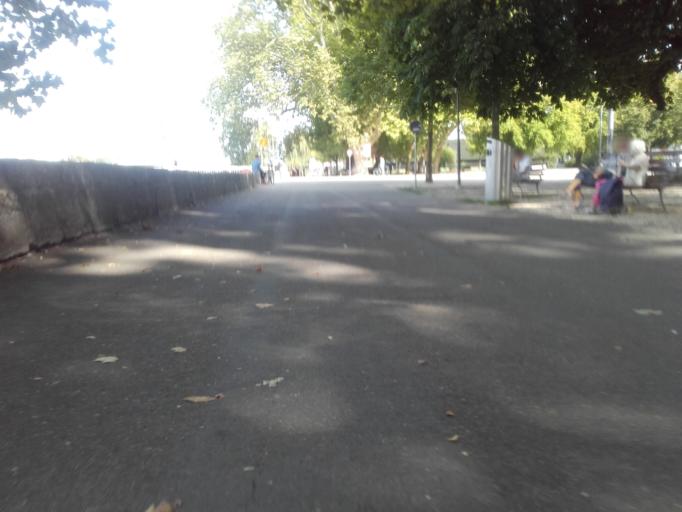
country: CH
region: Solothurn
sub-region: Bezirk Solothurn
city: Solothurn
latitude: 47.2058
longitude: 7.5390
